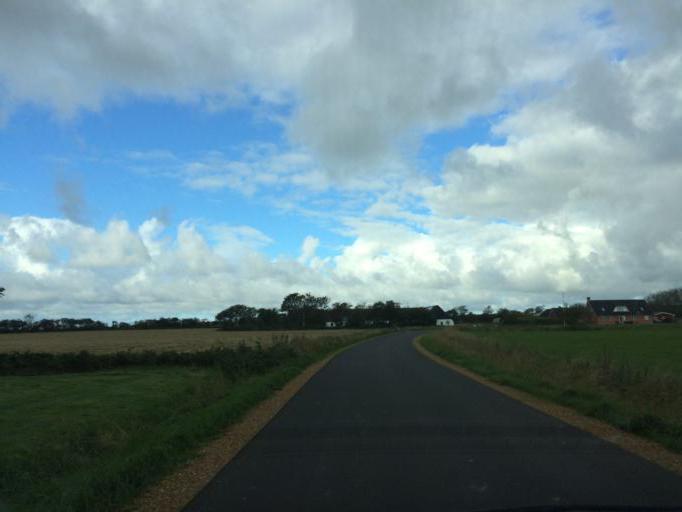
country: DK
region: Central Jutland
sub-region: Holstebro Kommune
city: Ulfborg
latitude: 56.2927
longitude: 8.3752
